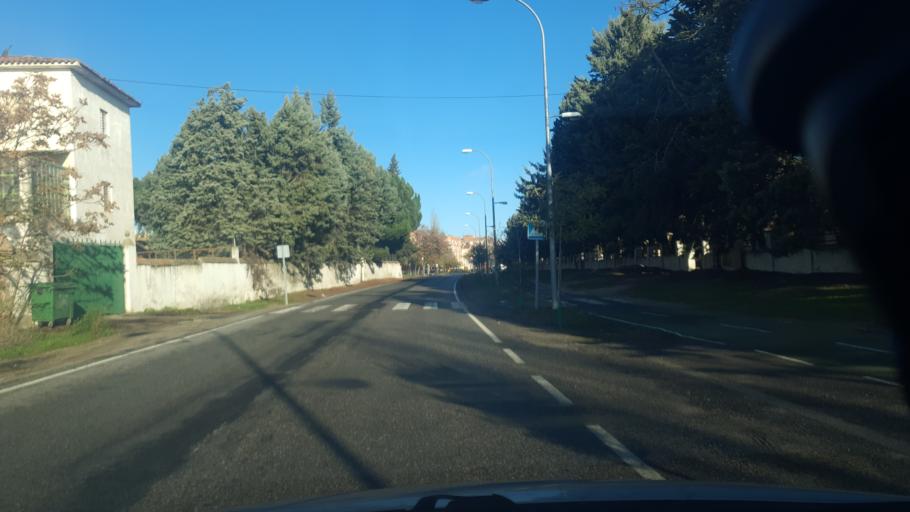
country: ES
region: Castille and Leon
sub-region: Provincia de Avila
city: Arevalo
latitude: 41.0521
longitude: -4.7196
